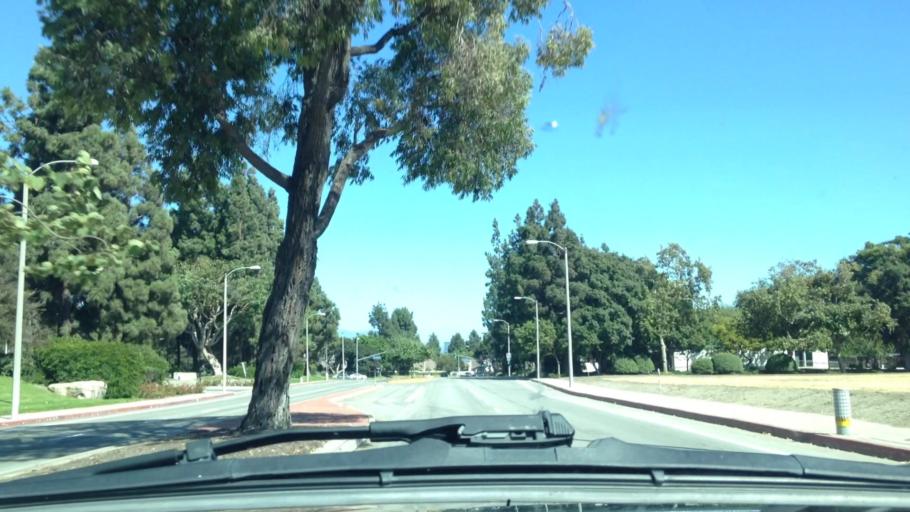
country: US
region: California
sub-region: Orange County
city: Fountain Valley
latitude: 33.6913
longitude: -117.9105
